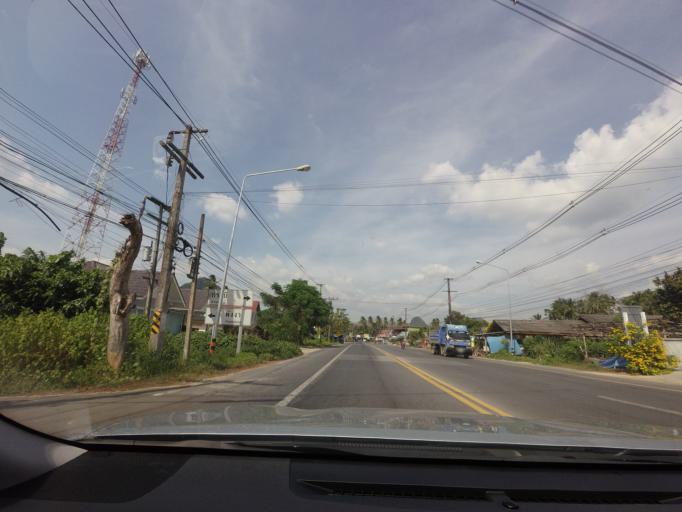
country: TH
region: Phangnga
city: Ban Ao Nang
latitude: 8.0907
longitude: 98.8107
